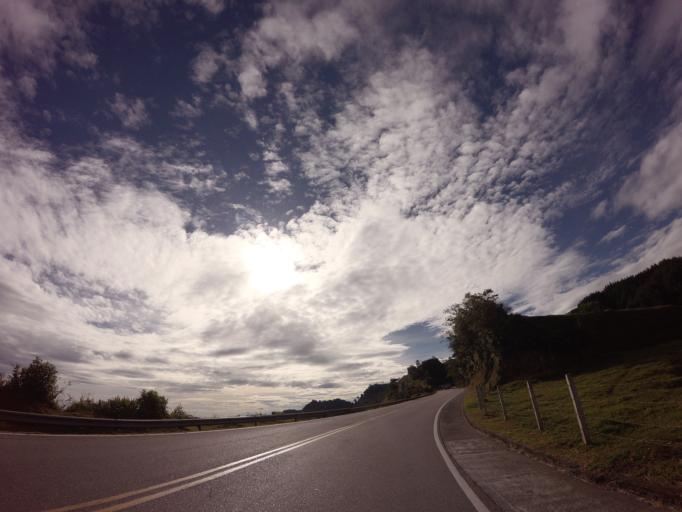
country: CO
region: Tolima
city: Casabianca
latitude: 5.1378
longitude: -75.1366
